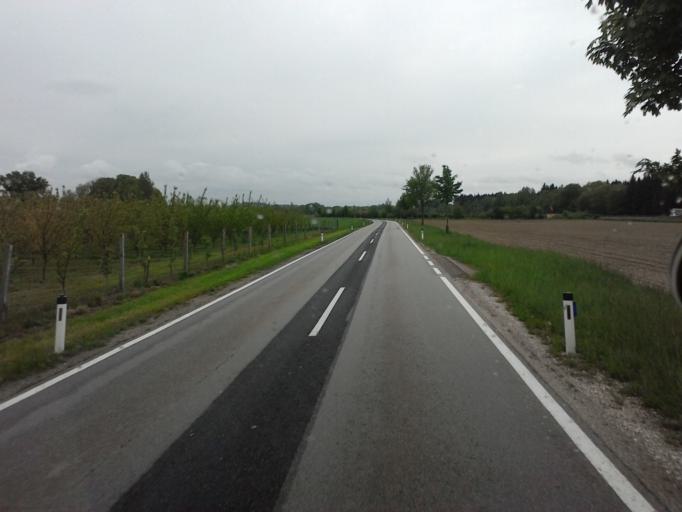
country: AT
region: Upper Austria
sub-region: Politischer Bezirk Scharding
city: Sankt Marienkirchen bei Schaerding
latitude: 48.3288
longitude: 13.4134
